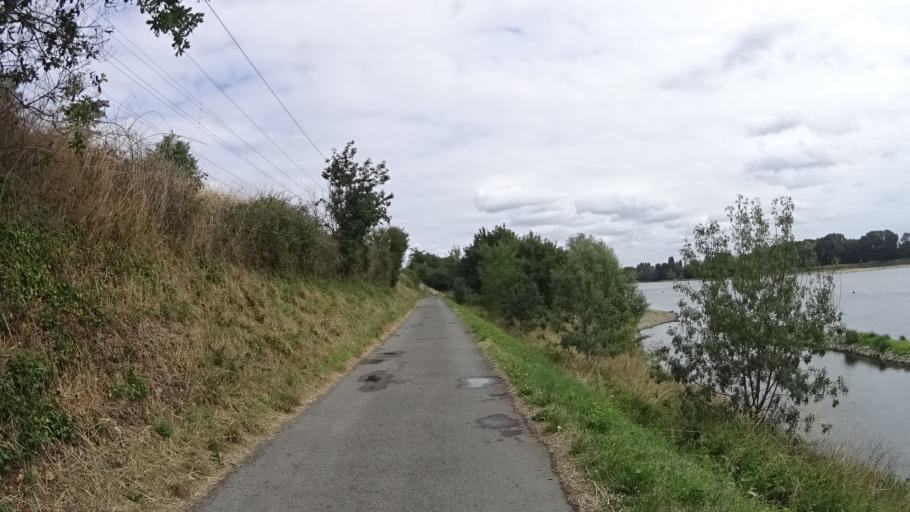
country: FR
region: Pays de la Loire
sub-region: Departement de Maine-et-Loire
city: Denee
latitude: 47.3978
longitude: -0.6276
